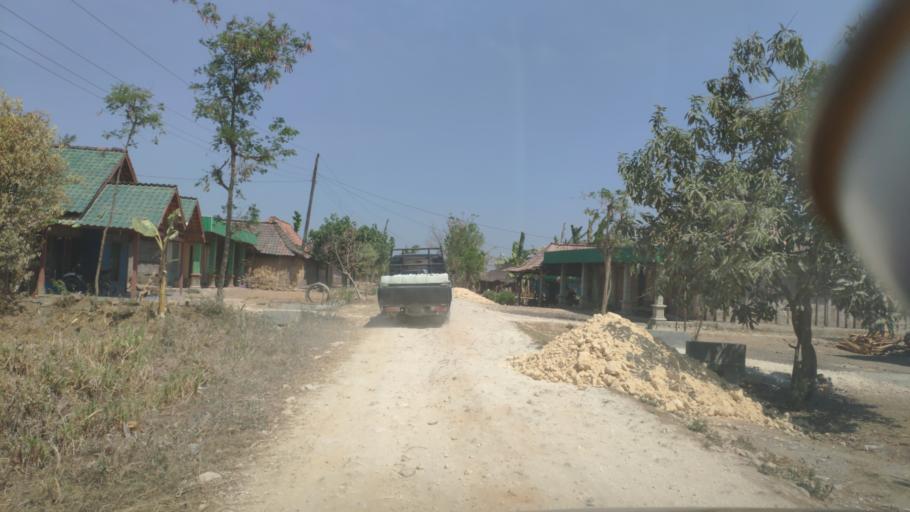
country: ID
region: Central Java
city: Pipes
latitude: -7.1085
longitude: 111.2830
